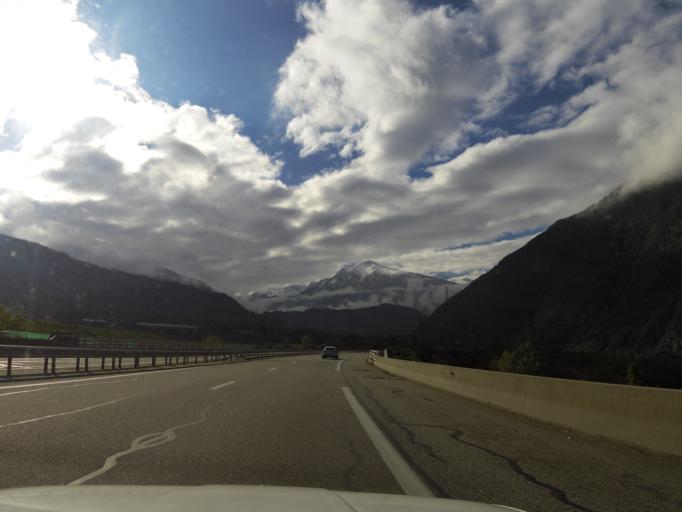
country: FR
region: Rhone-Alpes
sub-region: Departement de la Savoie
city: Saint-Michel-de-Maurienne
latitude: 45.2443
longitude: 6.4304
